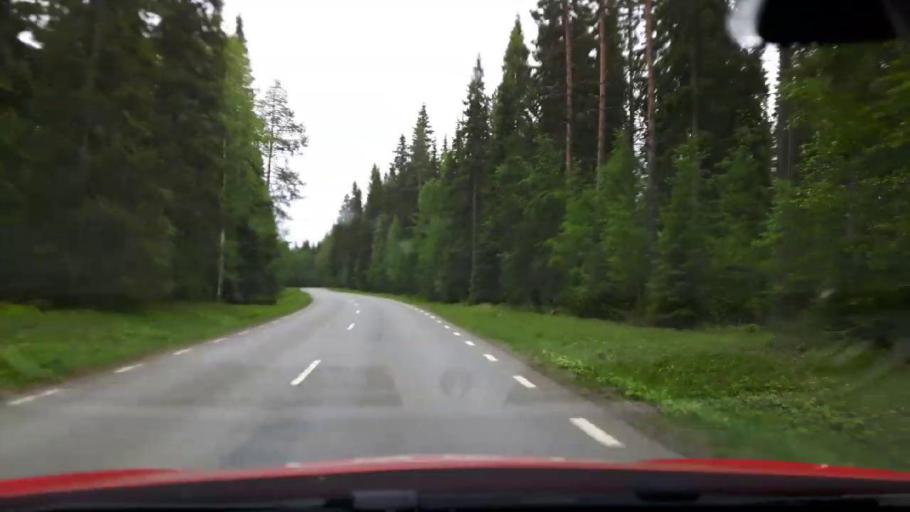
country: SE
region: Jaemtland
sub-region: Stroemsunds Kommun
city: Stroemsund
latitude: 63.4560
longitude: 15.4604
